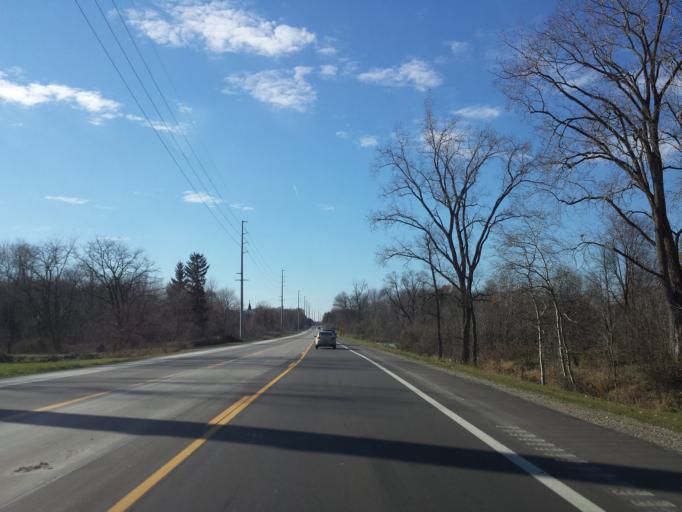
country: US
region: Michigan
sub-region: Livingston County
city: Brighton
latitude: 42.6315
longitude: -83.7921
